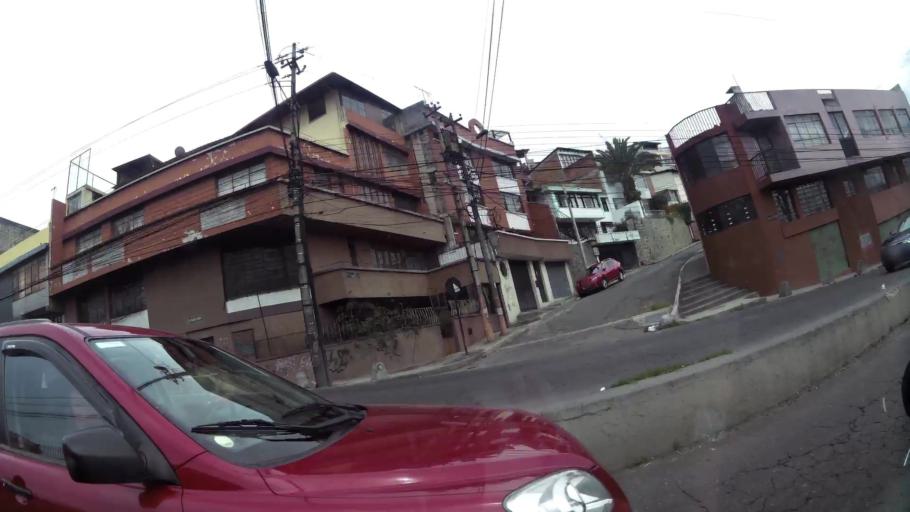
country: EC
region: Pichincha
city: Quito
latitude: -0.2161
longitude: -78.4911
